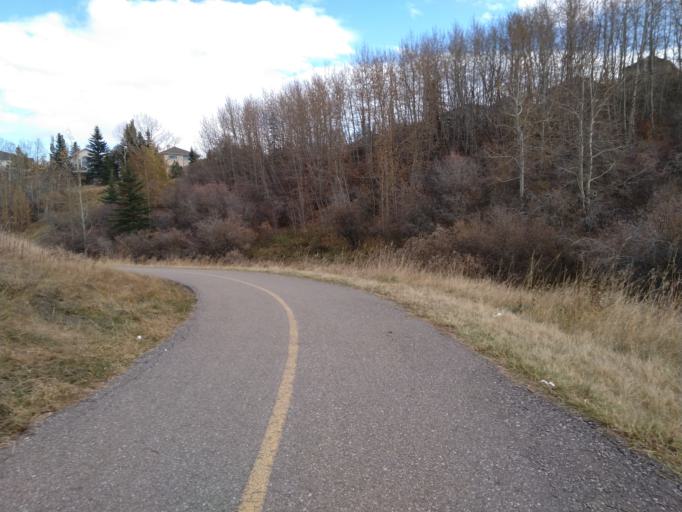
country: CA
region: Alberta
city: Calgary
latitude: 51.1362
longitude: -114.1389
